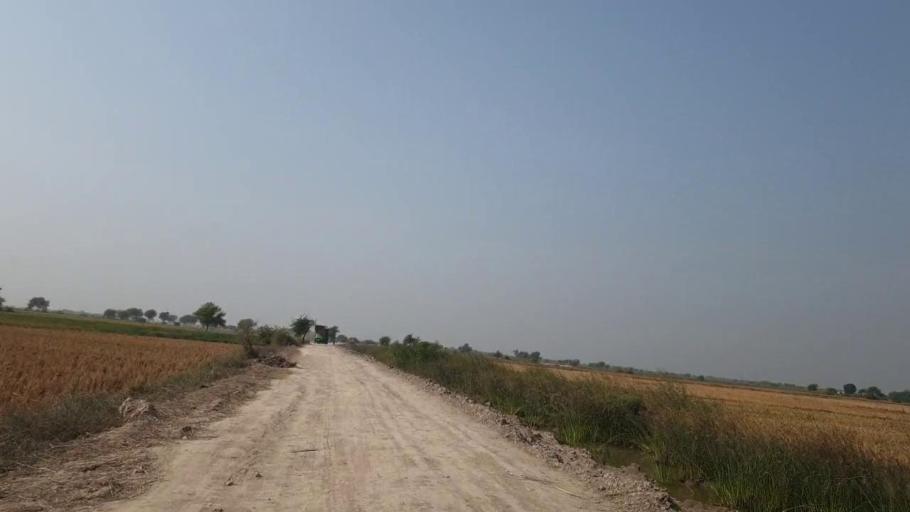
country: PK
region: Sindh
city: Kario
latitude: 24.9328
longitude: 68.5576
